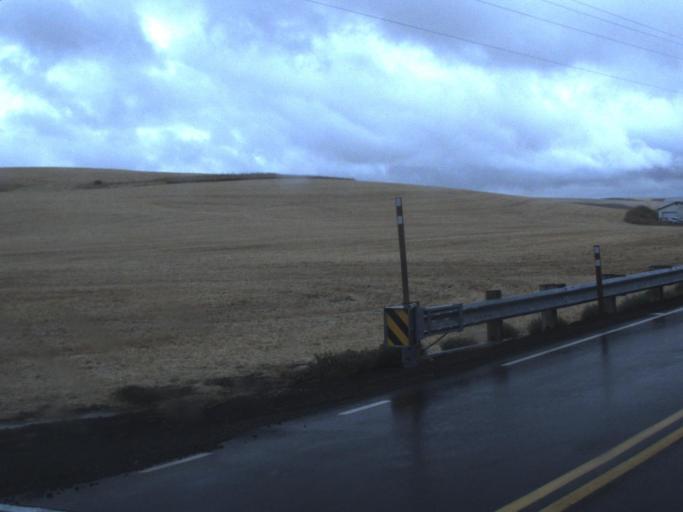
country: US
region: Washington
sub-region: Whitman County
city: Colfax
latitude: 47.0749
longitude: -117.5366
